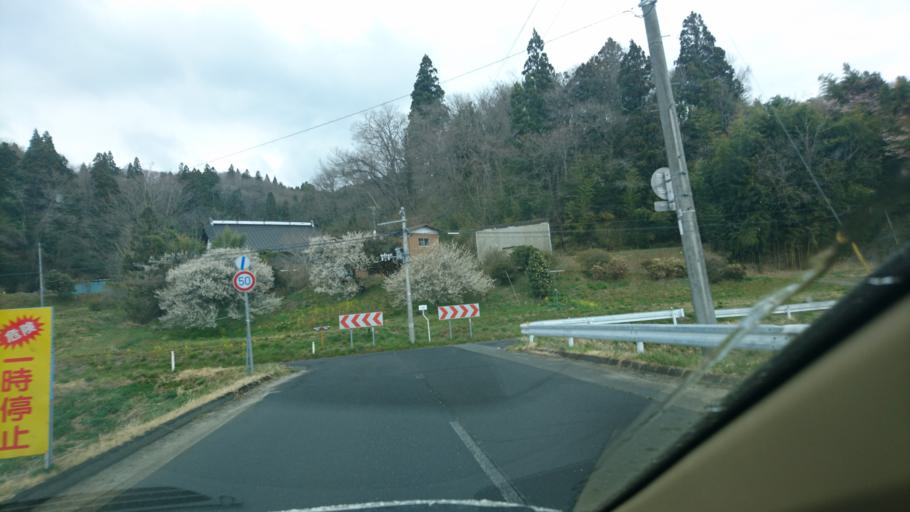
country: JP
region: Iwate
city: Ichinoseki
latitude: 38.9543
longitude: 141.3191
